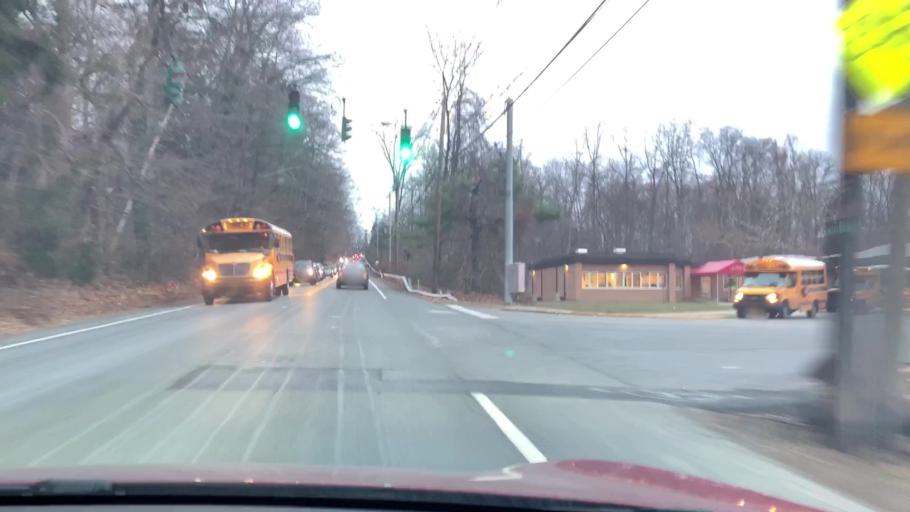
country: US
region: New York
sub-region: Rockland County
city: Sparkill
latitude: 41.0367
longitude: -73.9233
